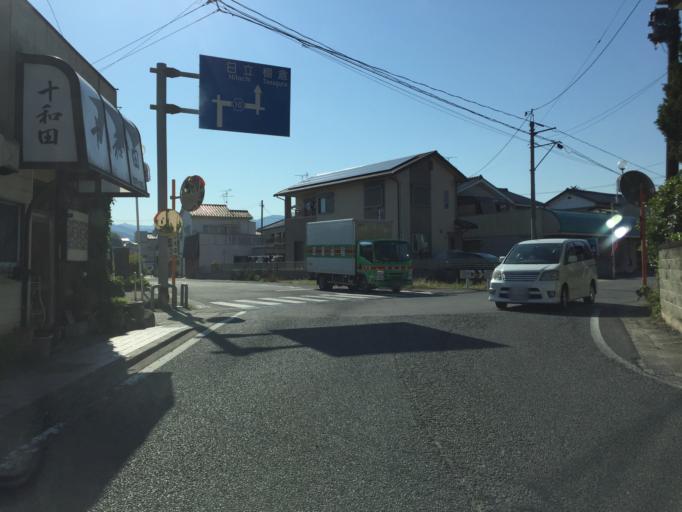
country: JP
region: Ibaraki
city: Kitaibaraki
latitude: 36.8916
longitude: 140.7609
